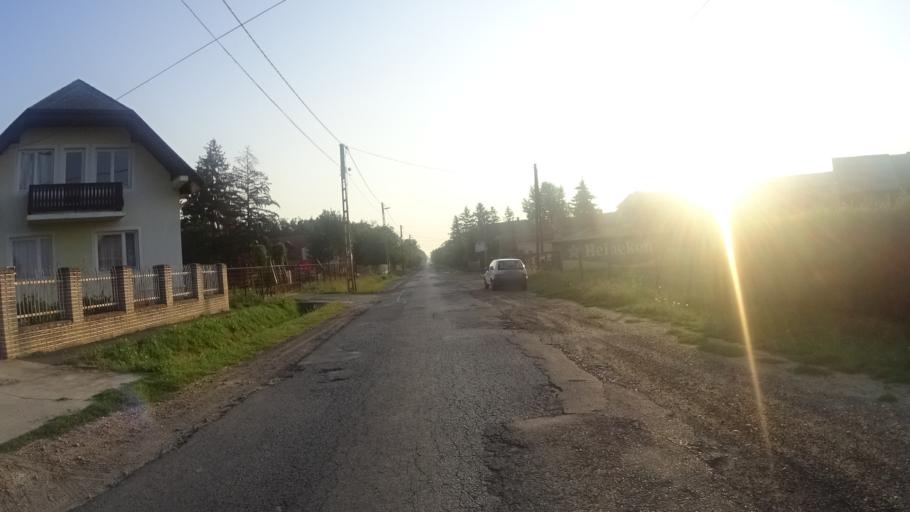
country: HU
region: Zala
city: Zalakomar
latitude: 46.5230
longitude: 17.1273
